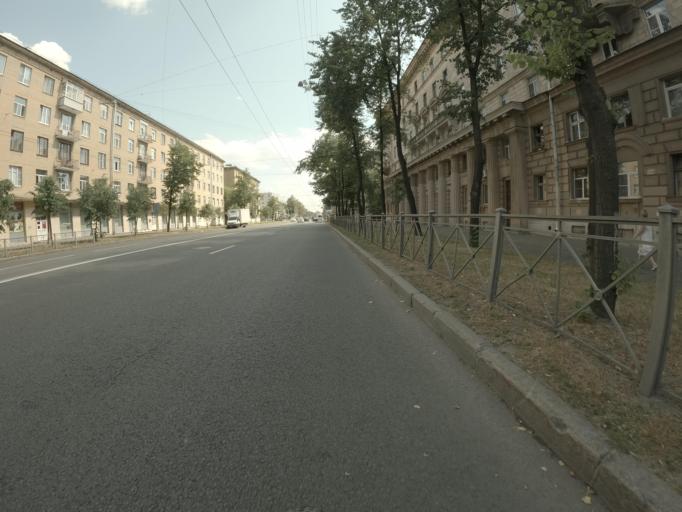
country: RU
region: St.-Petersburg
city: Avtovo
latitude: 59.8707
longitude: 30.2689
